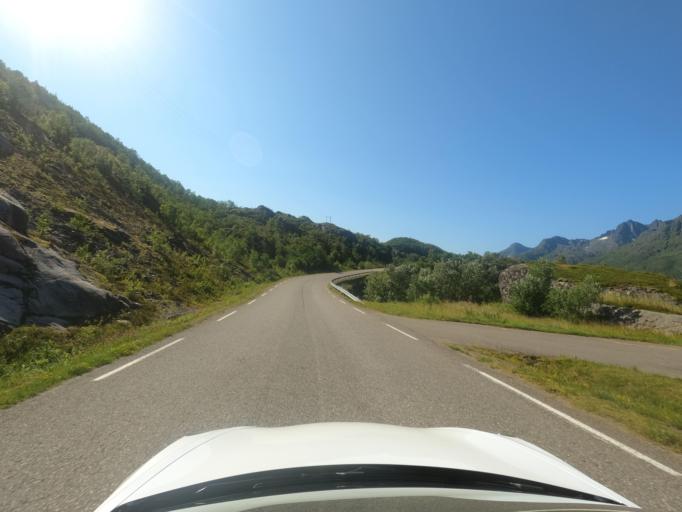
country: NO
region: Nordland
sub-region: Hadsel
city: Stokmarknes
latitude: 68.4388
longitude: 15.1855
